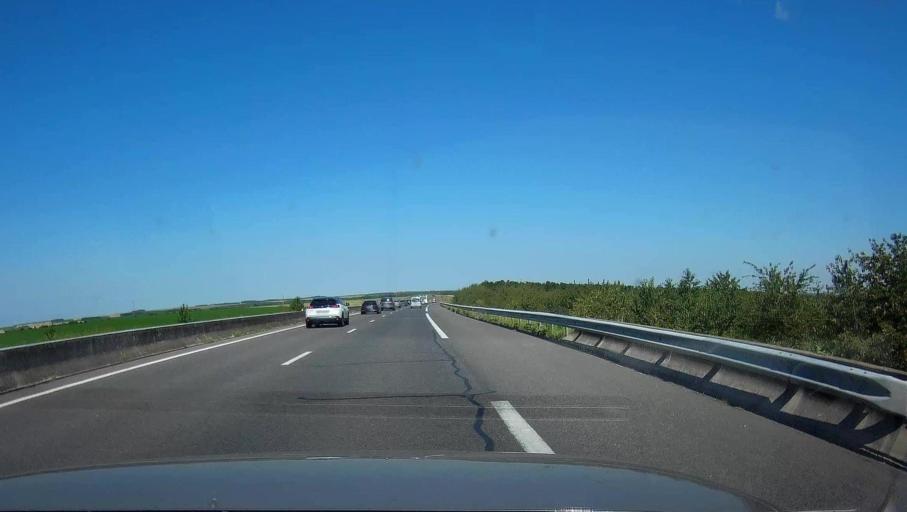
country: FR
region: Champagne-Ardenne
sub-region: Departement de la Marne
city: Compertrix
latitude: 48.8589
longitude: 4.2855
